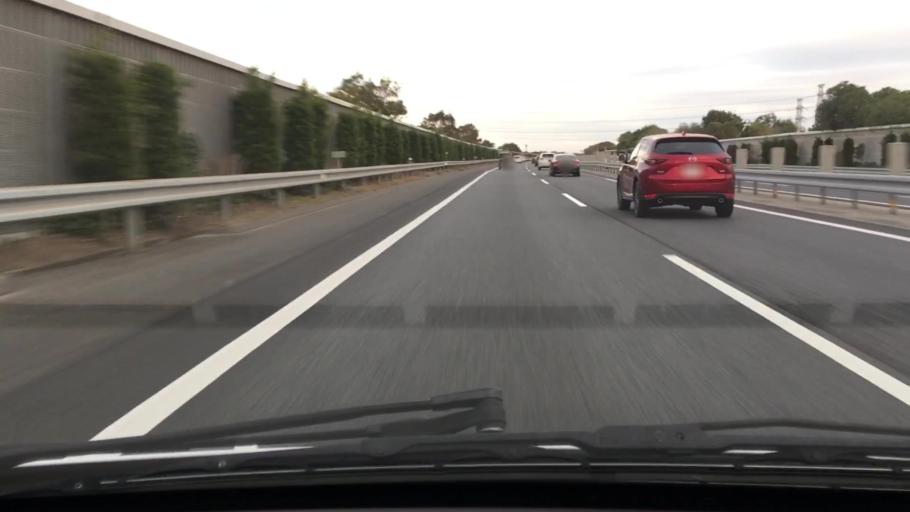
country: JP
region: Chiba
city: Ichihara
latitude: 35.5054
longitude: 140.1039
